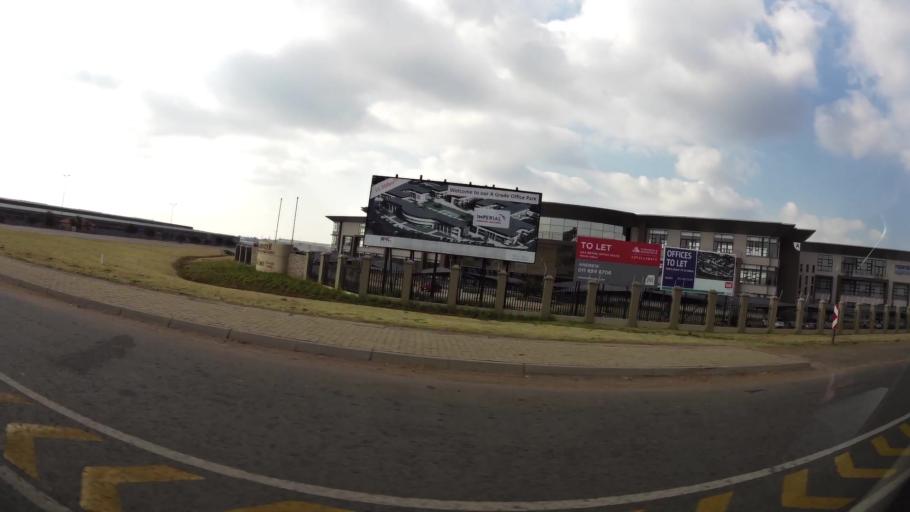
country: ZA
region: Gauteng
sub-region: Ekurhuleni Metropolitan Municipality
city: Benoni
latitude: -26.1406
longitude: 28.2690
